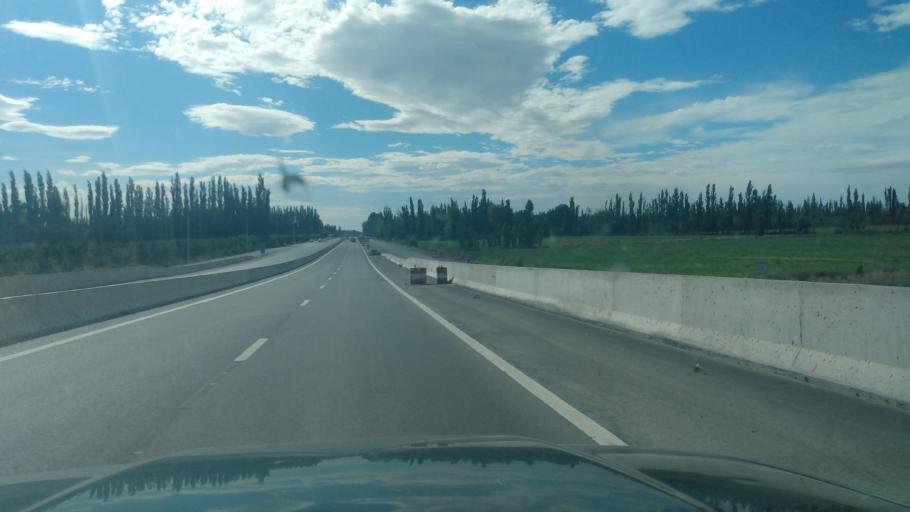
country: AR
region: Rio Negro
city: General Fernandez Oro
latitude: -38.9776
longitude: -67.9408
